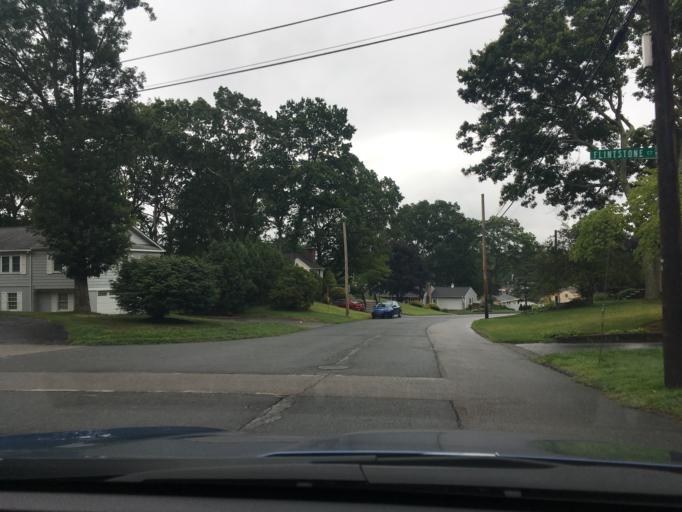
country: US
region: Rhode Island
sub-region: Kent County
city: East Greenwich
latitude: 41.6414
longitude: -71.4715
